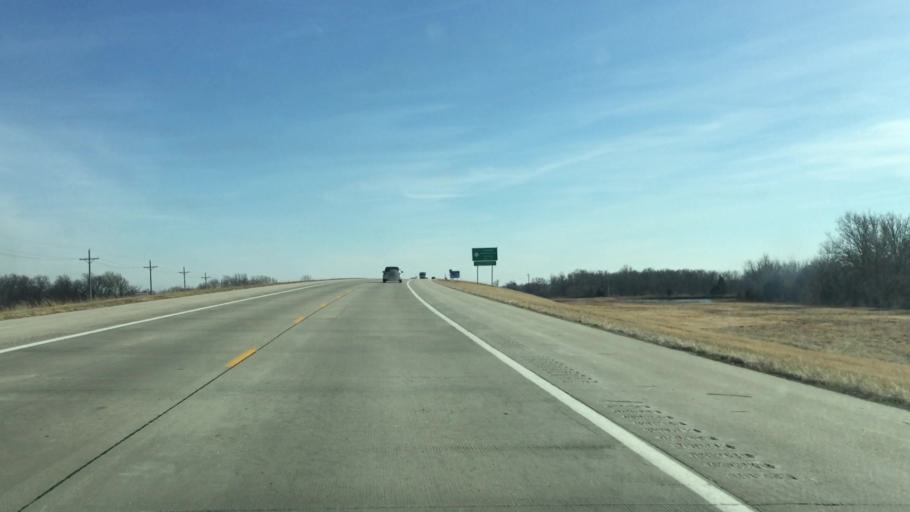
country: US
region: Kansas
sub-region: Labette County
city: Parsons
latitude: 37.3699
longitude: -95.2796
